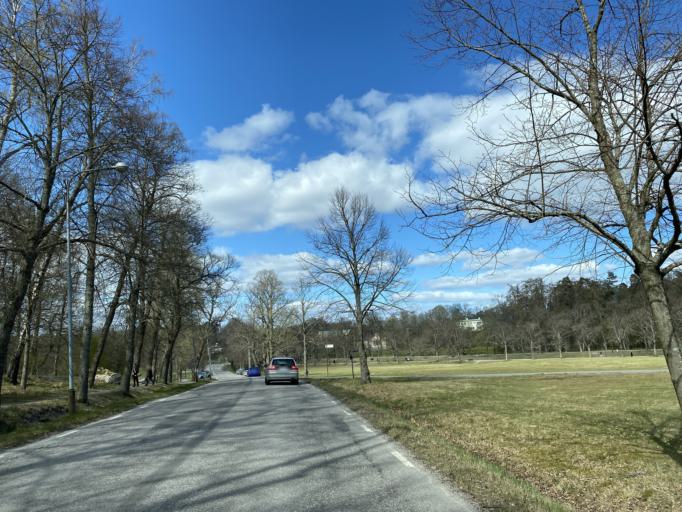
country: SE
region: Stockholm
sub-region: Nacka Kommun
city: Nacka
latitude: 59.3270
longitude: 18.1333
